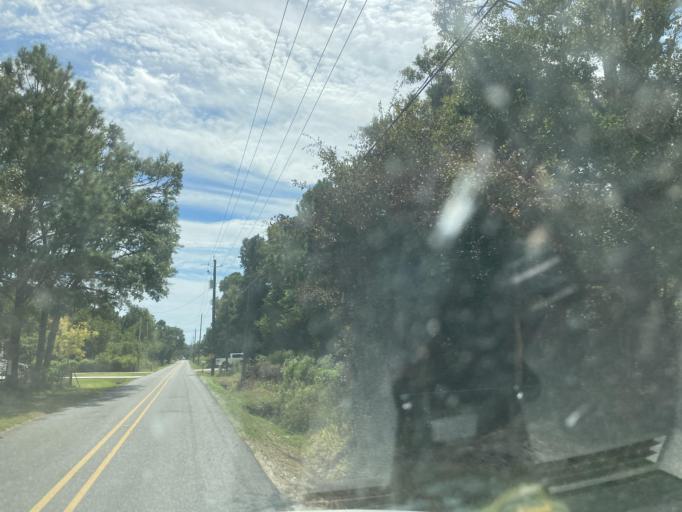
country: US
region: Mississippi
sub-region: Harrison County
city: D'Iberville
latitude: 30.4313
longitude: -88.8810
